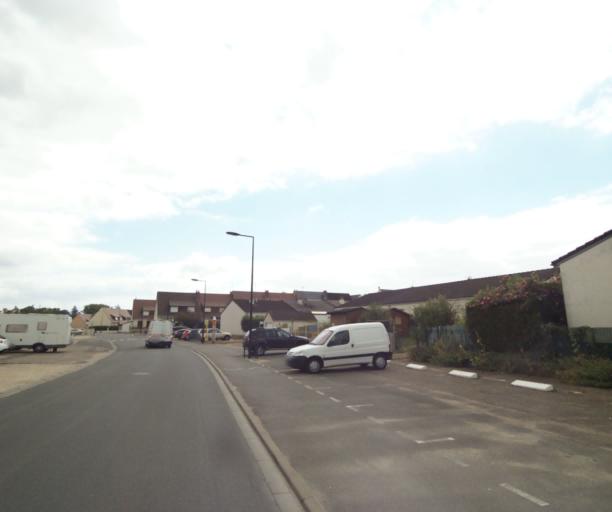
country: FR
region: Centre
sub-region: Departement du Loiret
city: Checy
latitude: 47.8933
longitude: 2.0268
